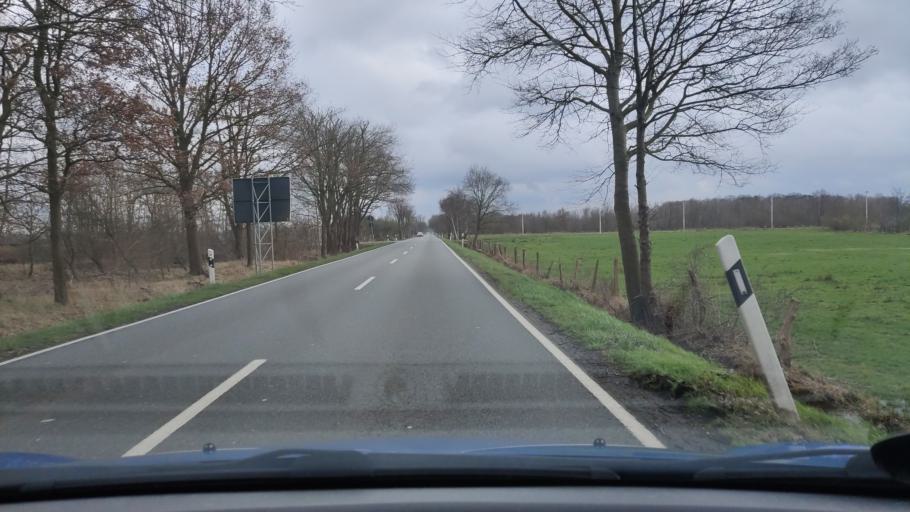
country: DE
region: Lower Saxony
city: Garbsen-Mitte
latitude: 52.4710
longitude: 9.6414
